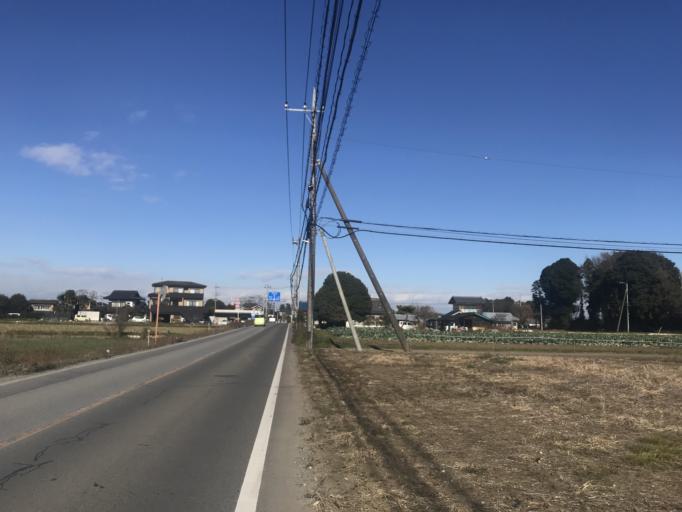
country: JP
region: Ibaraki
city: Yuki
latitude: 36.3667
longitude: 139.8772
